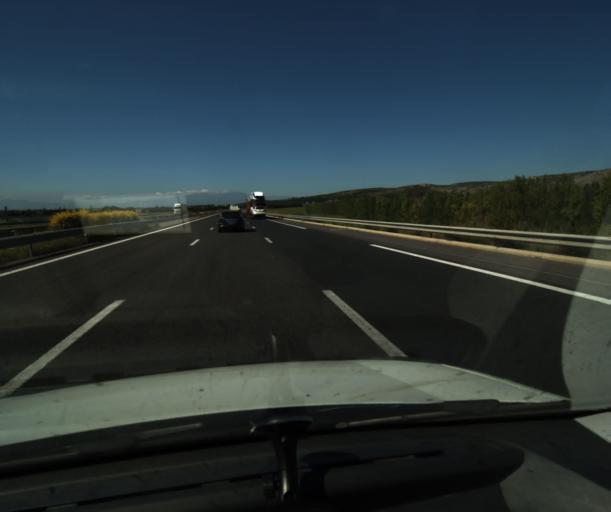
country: FR
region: Languedoc-Roussillon
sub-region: Departement des Pyrenees-Orientales
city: Salses-le-Chateau
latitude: 42.8506
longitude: 2.9330
